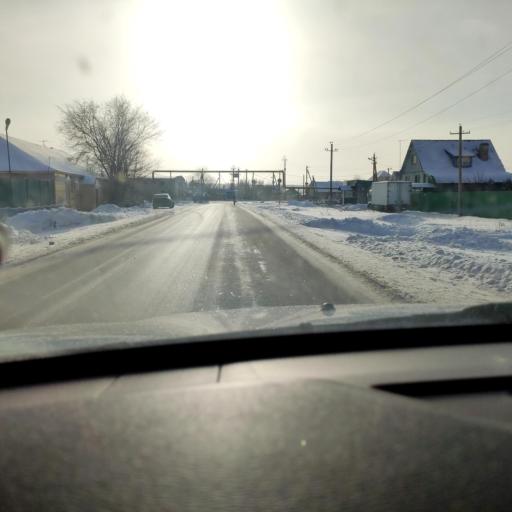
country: RU
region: Samara
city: Smyshlyayevka
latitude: 53.1614
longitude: 50.3825
